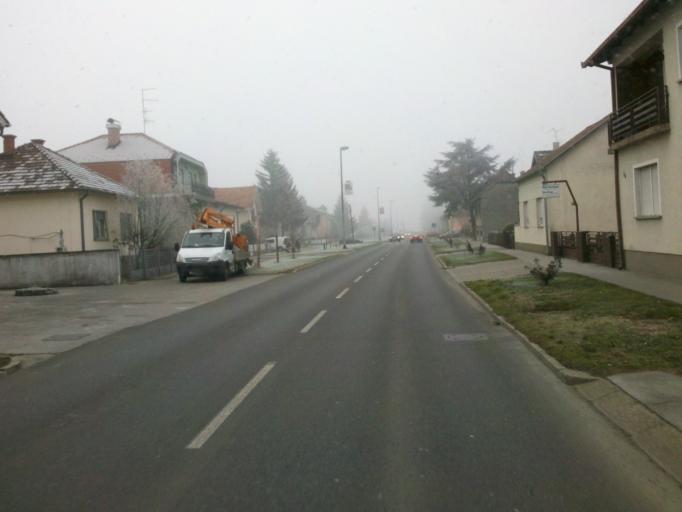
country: HR
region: Medimurska
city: Cakovec
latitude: 46.3815
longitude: 16.4297
